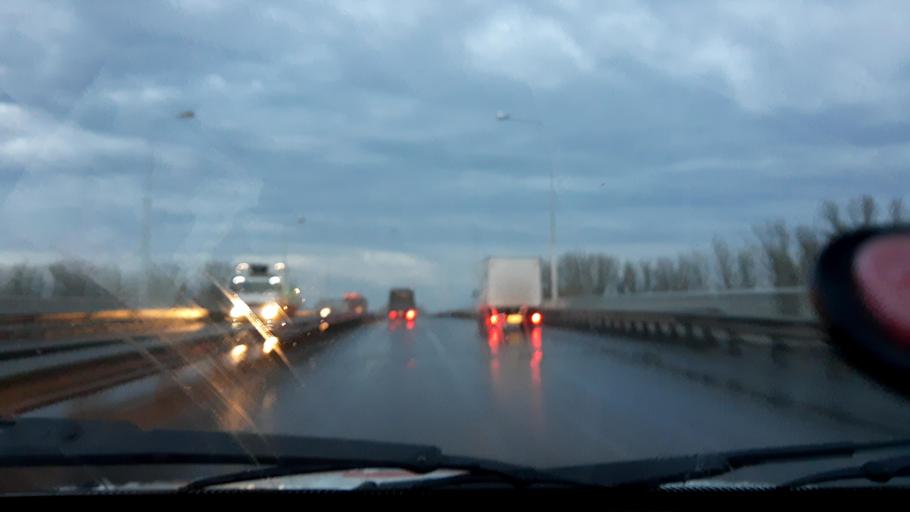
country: RU
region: Bashkortostan
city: Iglino
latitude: 54.7892
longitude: 56.2156
